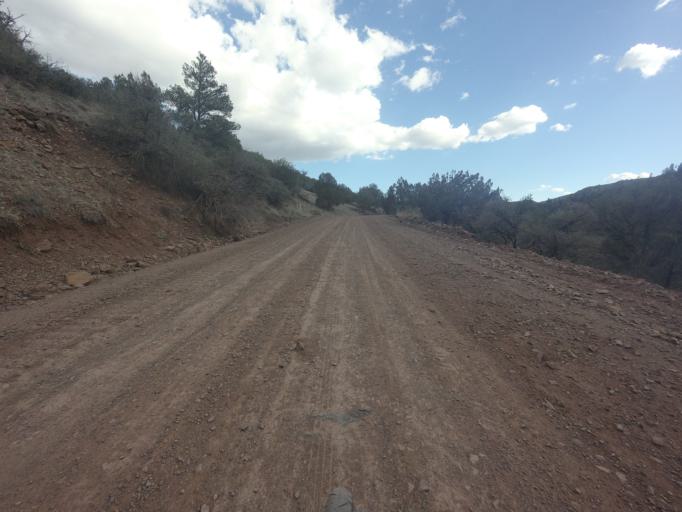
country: US
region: Arizona
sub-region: Yavapai County
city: Camp Verde
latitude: 34.4506
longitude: -111.6932
